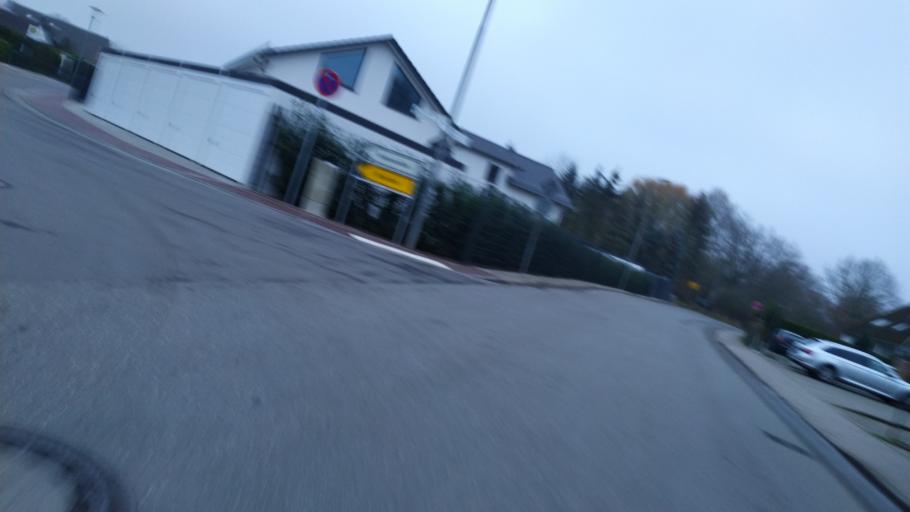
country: DE
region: Schleswig-Holstein
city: Travemuende
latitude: 53.9882
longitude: 10.8401
